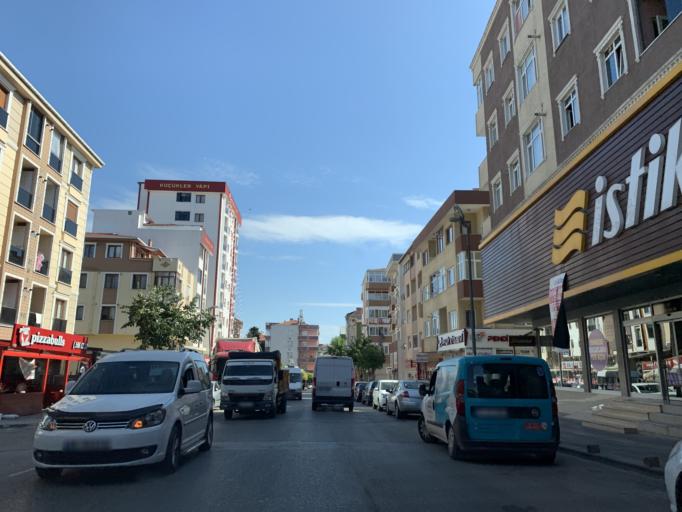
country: TR
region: Istanbul
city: Pendik
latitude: 40.8801
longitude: 29.2726
